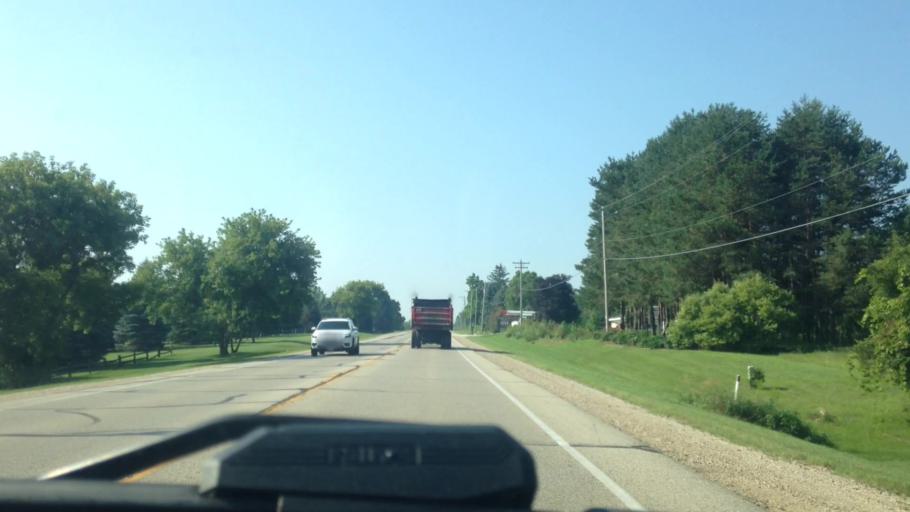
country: US
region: Wisconsin
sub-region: Waukesha County
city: Merton
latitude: 43.1743
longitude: -88.2624
